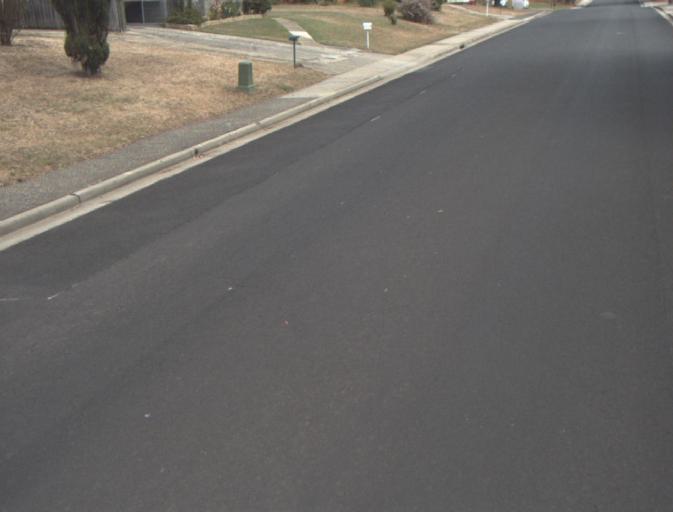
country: AU
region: Tasmania
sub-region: Launceston
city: Newstead
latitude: -41.4139
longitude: 147.1715
